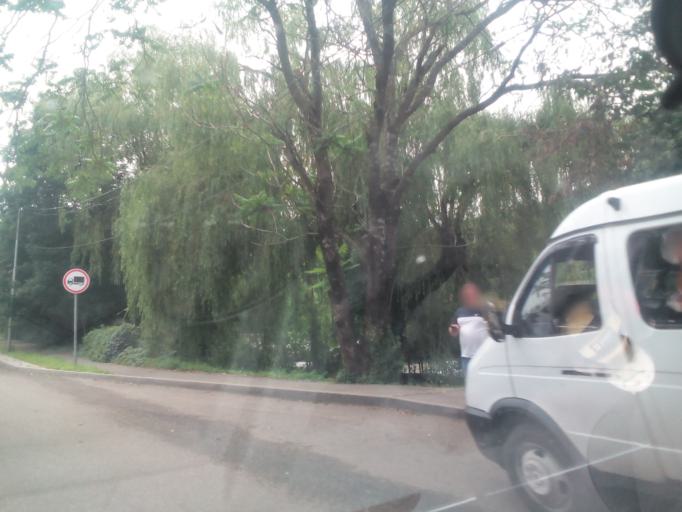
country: RU
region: Stavropol'skiy
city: Zheleznovodsk
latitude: 44.1398
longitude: 43.0127
